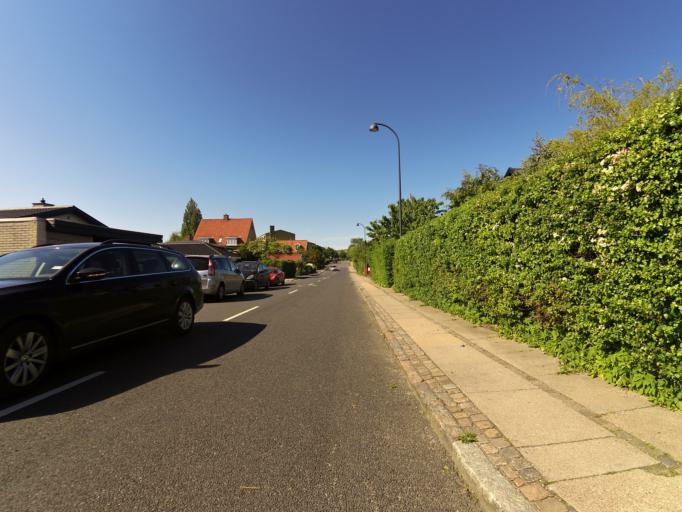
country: DK
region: Capital Region
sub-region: Gladsaxe Municipality
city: Buddinge
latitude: 55.7337
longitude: 12.5200
